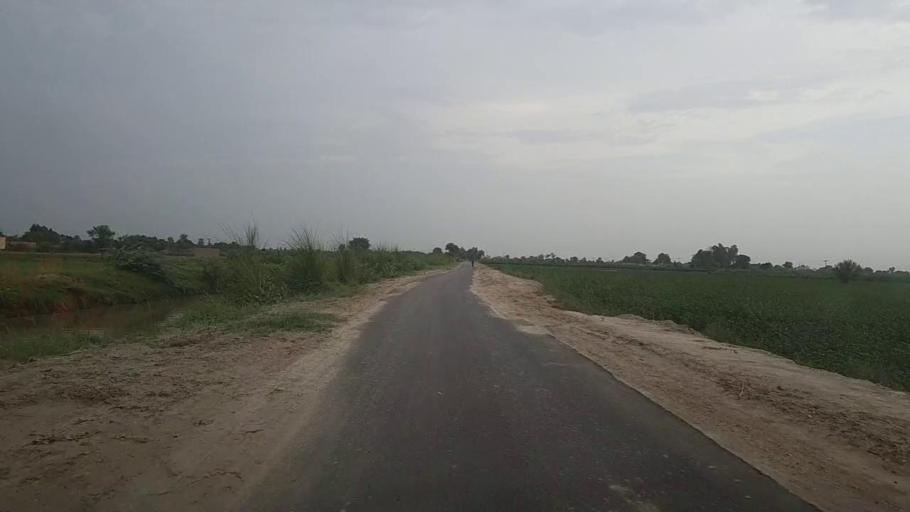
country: PK
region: Sindh
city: Karaundi
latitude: 26.9875
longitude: 68.3537
